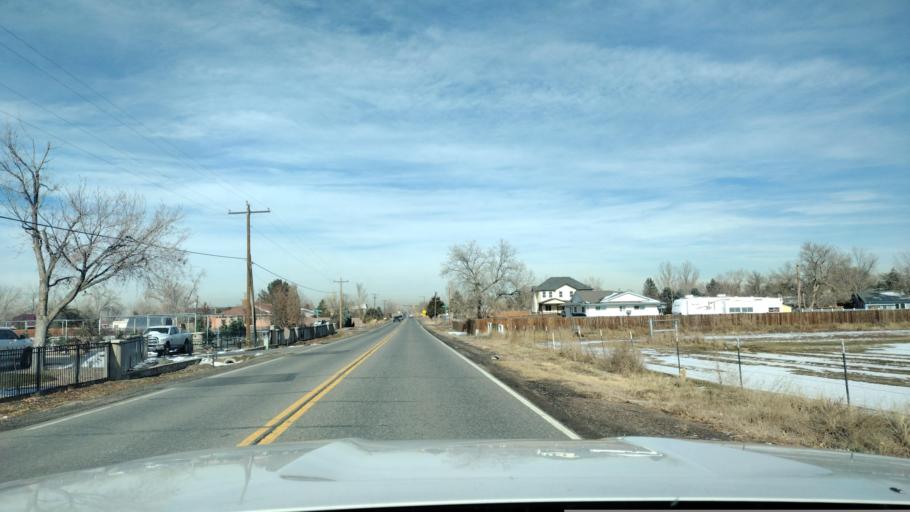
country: US
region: Colorado
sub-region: Adams County
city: Brighton
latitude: 39.9396
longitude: -104.8183
